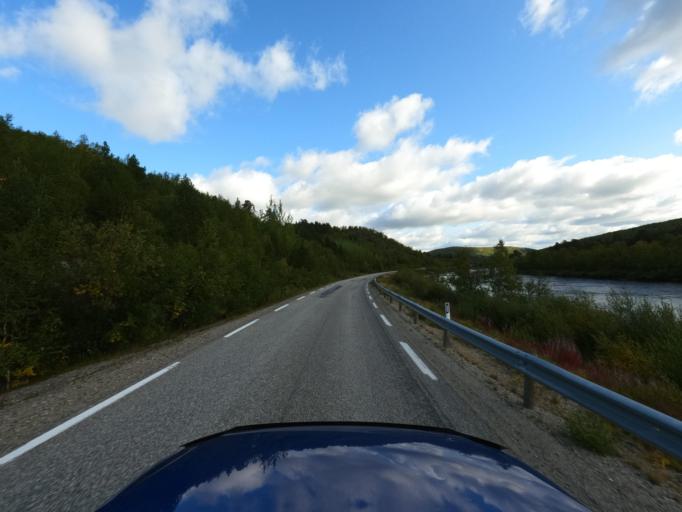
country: NO
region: Finnmark Fylke
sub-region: Porsanger
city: Lakselv
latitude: 69.4260
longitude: 24.8619
